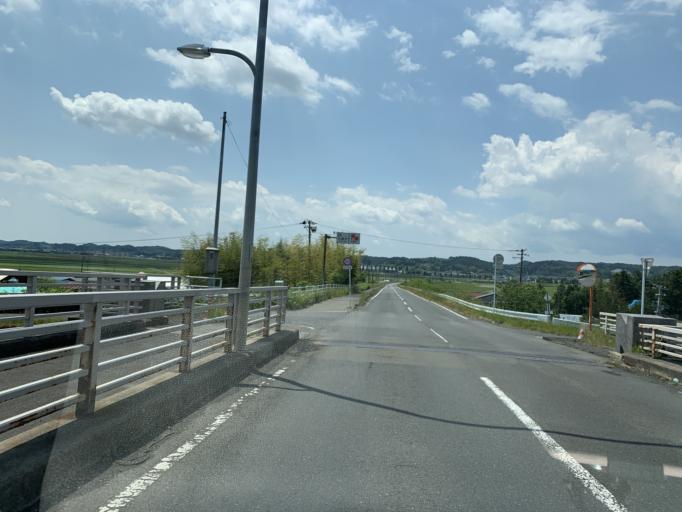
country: JP
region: Miyagi
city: Kogota
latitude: 38.5269
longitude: 141.0580
